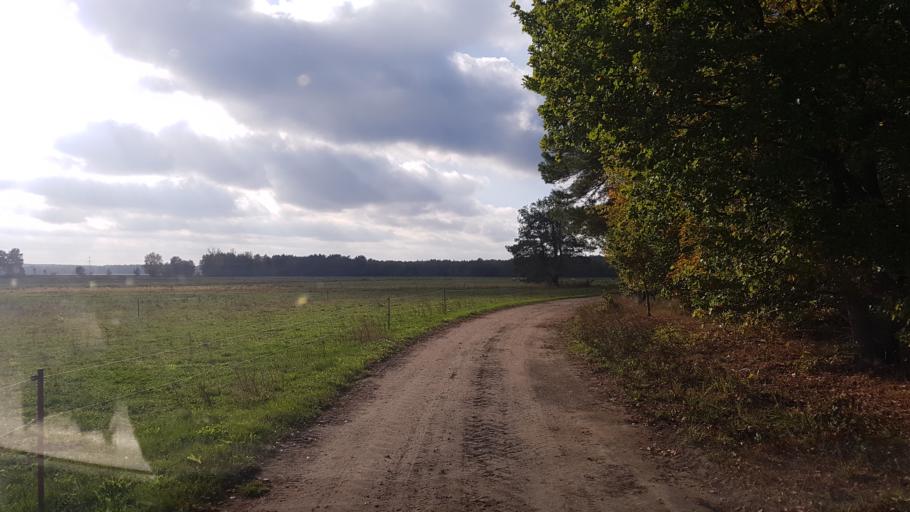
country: DE
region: Brandenburg
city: Schonborn
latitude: 51.5765
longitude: 13.5061
